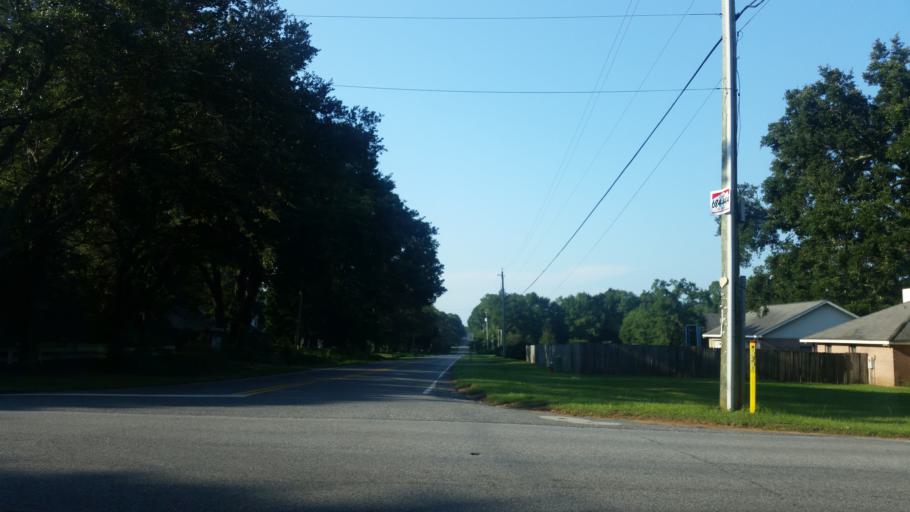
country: US
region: Florida
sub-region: Escambia County
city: Ensley
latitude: 30.5199
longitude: -87.3220
